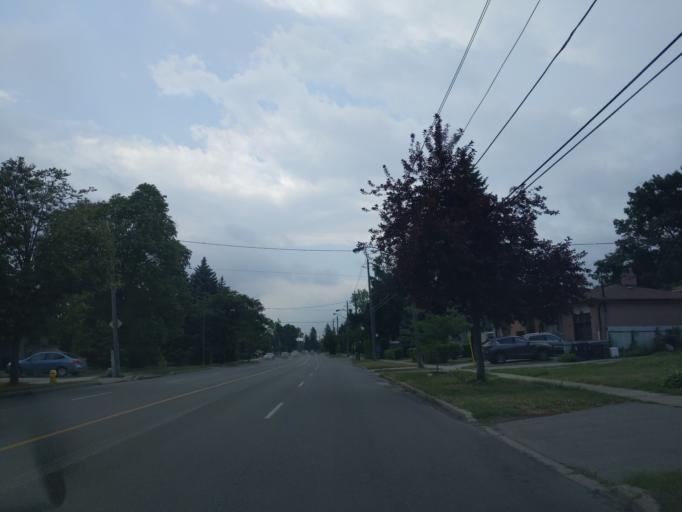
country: CA
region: Ontario
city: North York
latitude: 43.7925
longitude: -79.4118
